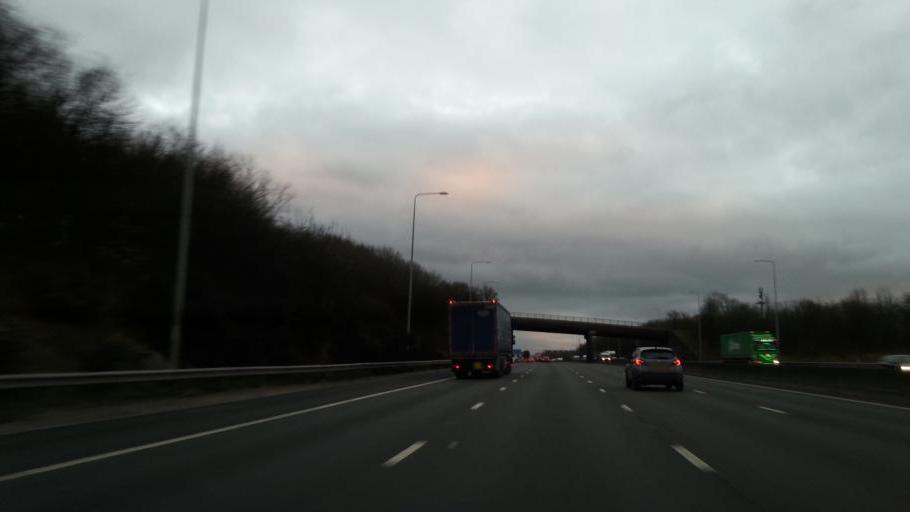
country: GB
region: England
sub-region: Derbyshire
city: Pinxton
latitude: 53.0820
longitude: -1.2967
